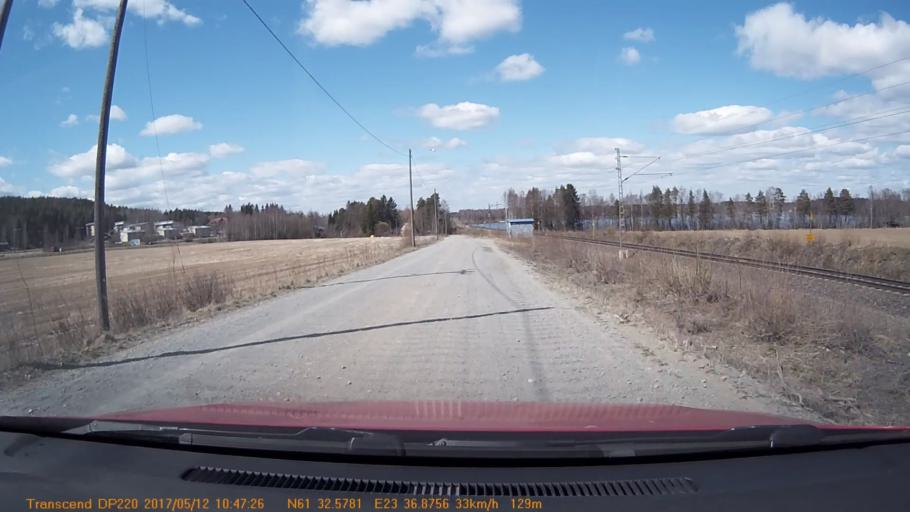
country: FI
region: Pirkanmaa
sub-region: Tampere
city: Yloejaervi
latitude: 61.5429
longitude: 23.6148
